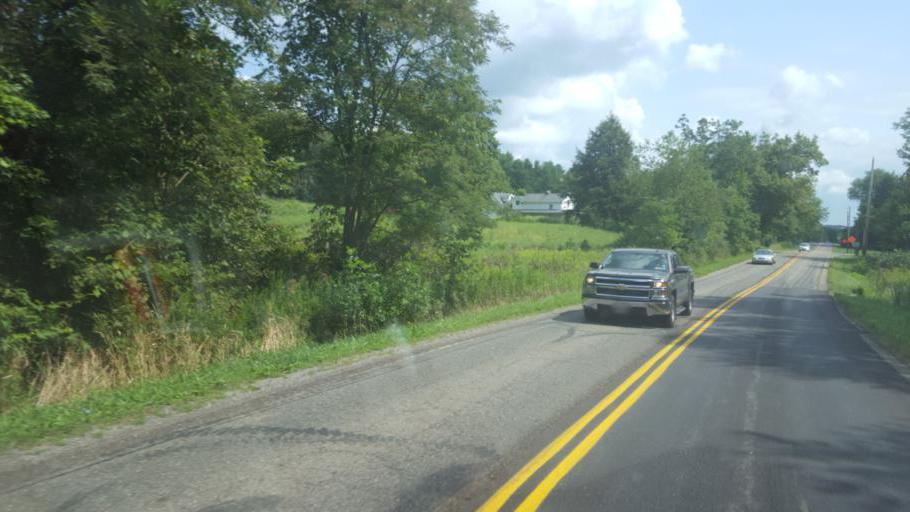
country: US
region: Ohio
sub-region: Columbiana County
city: New Waterford
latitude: 40.7961
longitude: -80.6669
